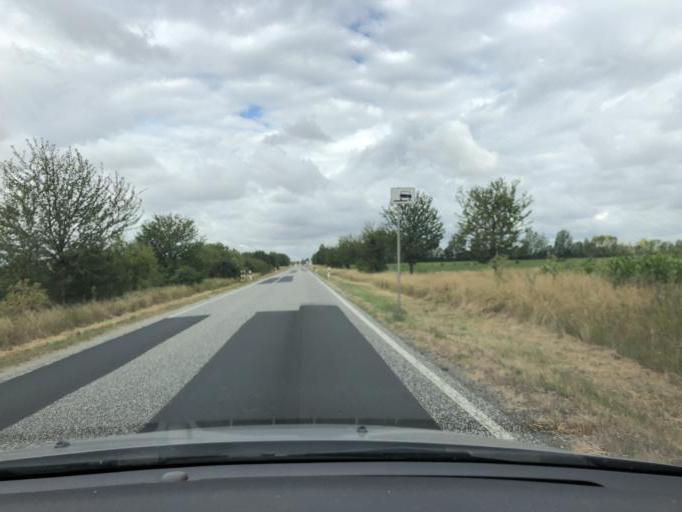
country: DE
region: Saxony-Anhalt
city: Bad Lauchstadt
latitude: 51.4265
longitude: 11.8586
